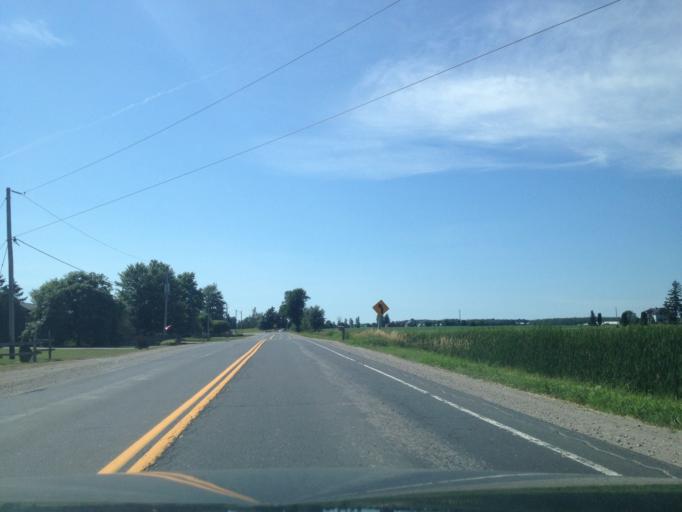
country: CA
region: Ontario
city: Stratford
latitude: 43.5019
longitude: -80.8783
